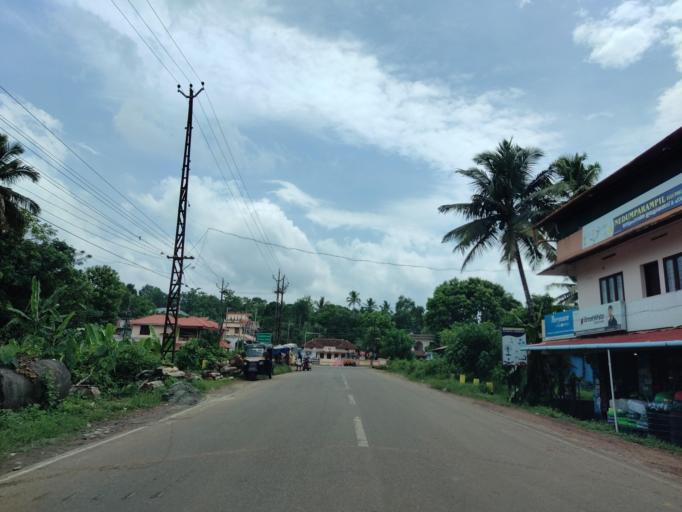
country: IN
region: Kerala
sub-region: Alappuzha
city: Mavelikara
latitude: 9.2261
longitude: 76.6168
